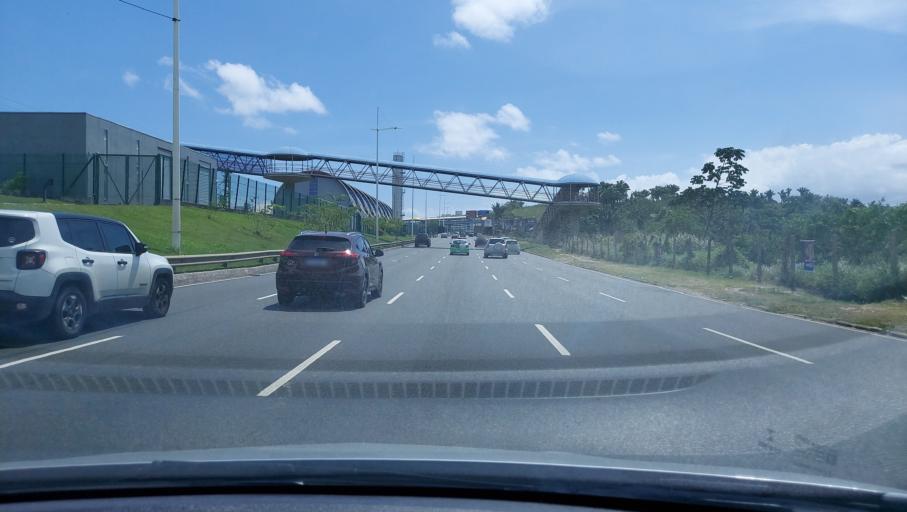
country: BR
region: Bahia
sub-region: Lauro De Freitas
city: Lauro de Freitas
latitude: -12.9329
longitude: -38.3930
